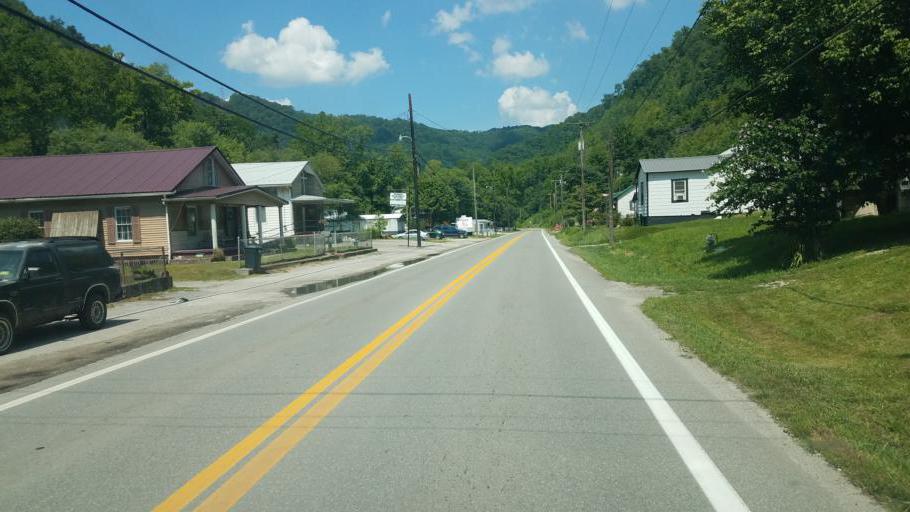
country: US
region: West Virginia
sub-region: Kanawha County
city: Chesapeake
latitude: 38.1646
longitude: -81.4504
